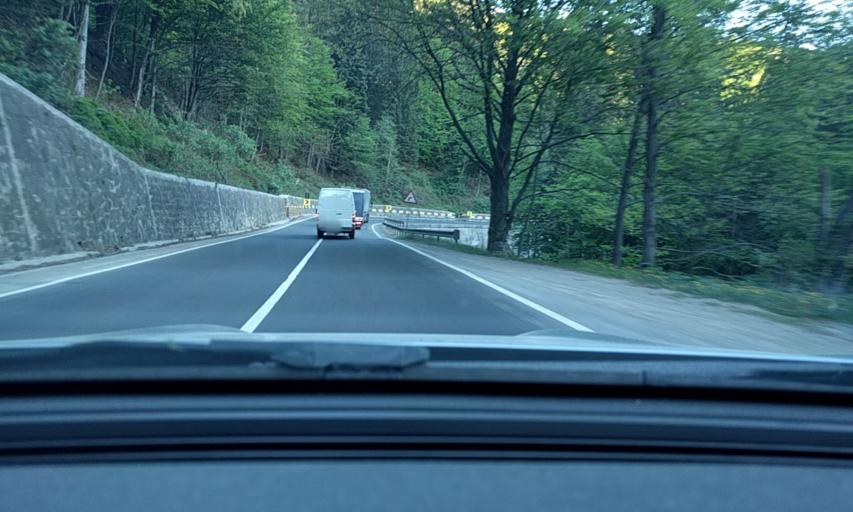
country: RO
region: Covasna
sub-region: Comuna Bretcu
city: Bretcu
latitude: 46.0820
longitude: 26.3972
